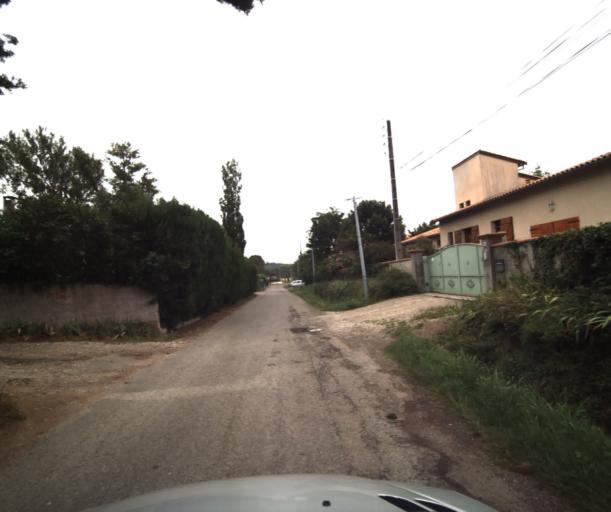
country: FR
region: Midi-Pyrenees
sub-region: Departement de la Haute-Garonne
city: Labarthe-sur-Leze
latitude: 43.4675
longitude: 1.3989
